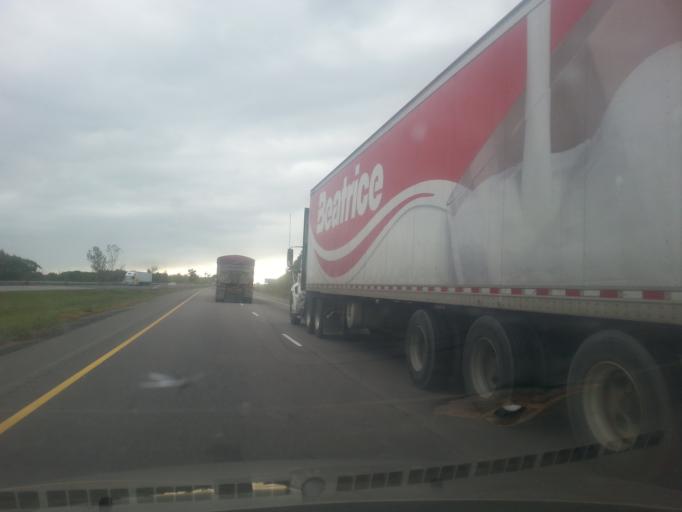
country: CA
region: Ontario
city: Quinte West
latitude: 44.0829
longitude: -77.7276
